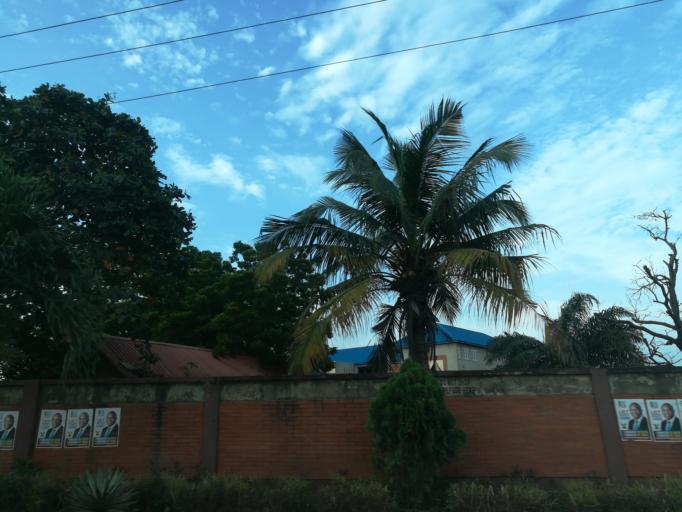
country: NG
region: Lagos
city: Ebute Ikorodu
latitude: 6.6142
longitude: 3.4769
